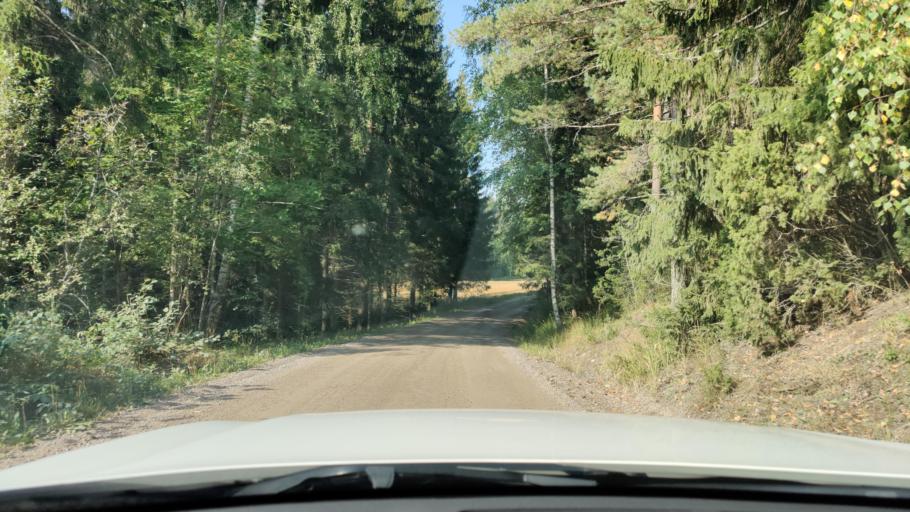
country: FI
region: Haeme
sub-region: Haemeenlinna
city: Tervakoski
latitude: 60.6766
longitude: 24.5982
